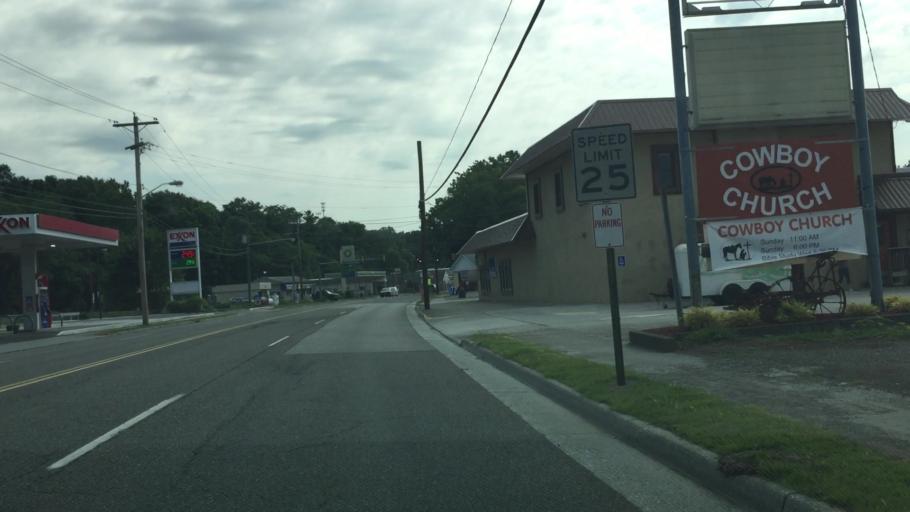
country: US
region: Virginia
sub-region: Pulaski County
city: Pulaski
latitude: 37.0483
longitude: -80.7723
